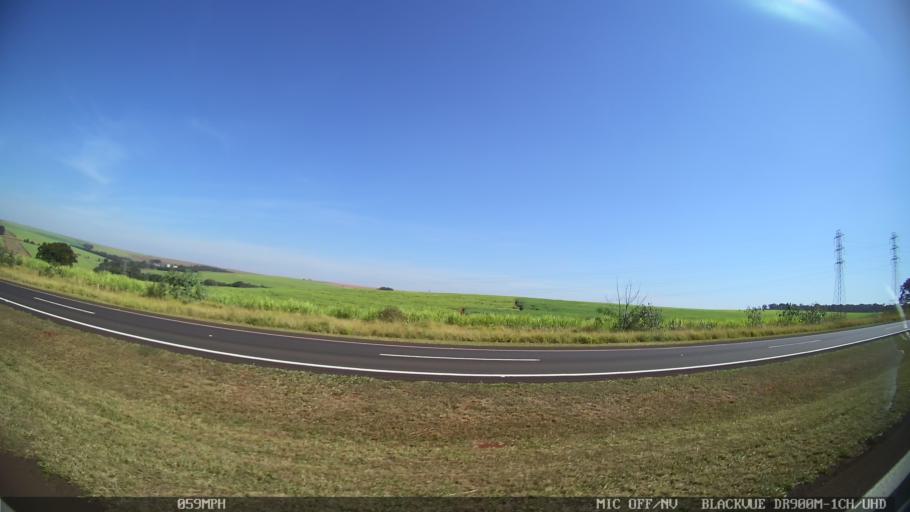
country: BR
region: Sao Paulo
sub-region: Ribeirao Preto
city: Ribeirao Preto
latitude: -21.1899
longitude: -47.8867
